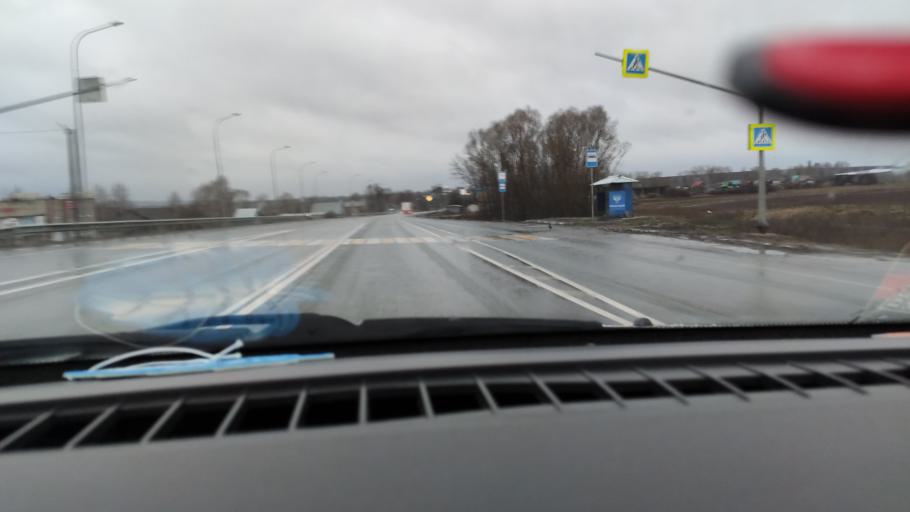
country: RU
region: Tatarstan
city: Mendeleyevsk
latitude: 56.0329
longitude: 52.3795
